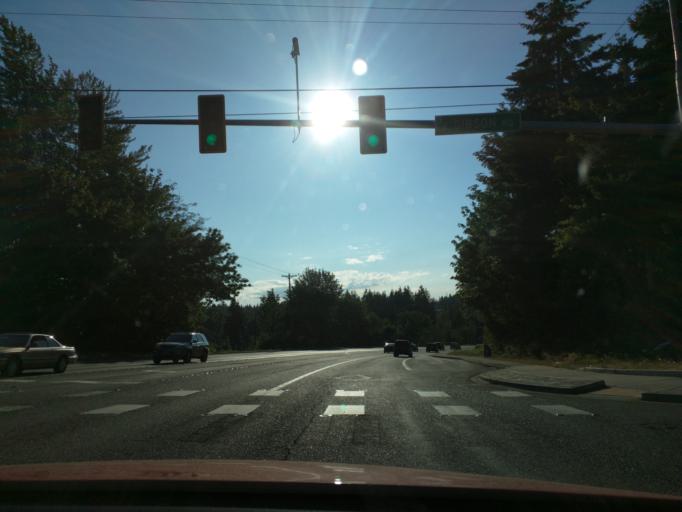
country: US
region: Washington
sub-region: Snohomish County
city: Martha Lake
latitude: 47.8820
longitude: -122.2503
